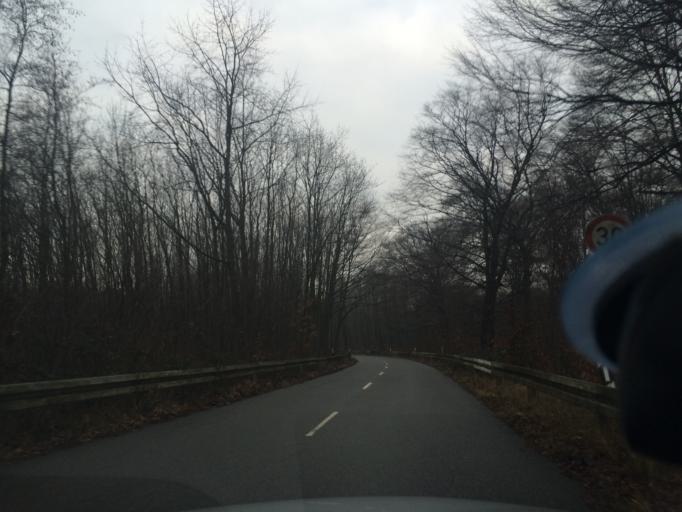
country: DE
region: Hesse
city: Morfelden-Walldorf
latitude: 50.0357
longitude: 8.6014
